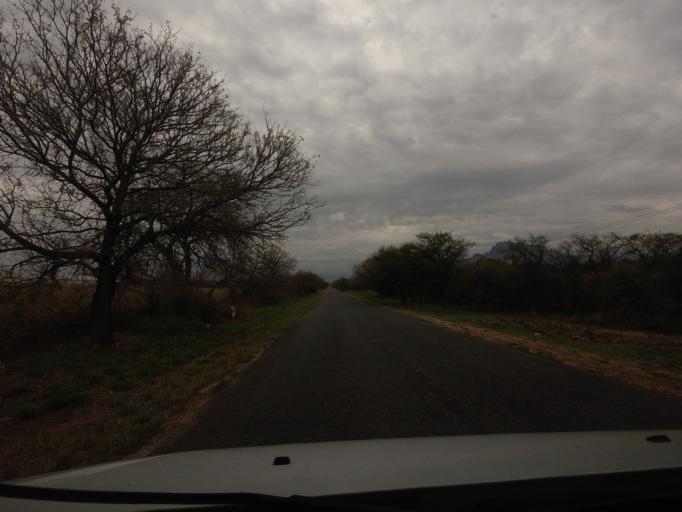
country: ZA
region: Limpopo
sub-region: Mopani District Municipality
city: Hoedspruit
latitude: -24.4527
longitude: 30.8631
